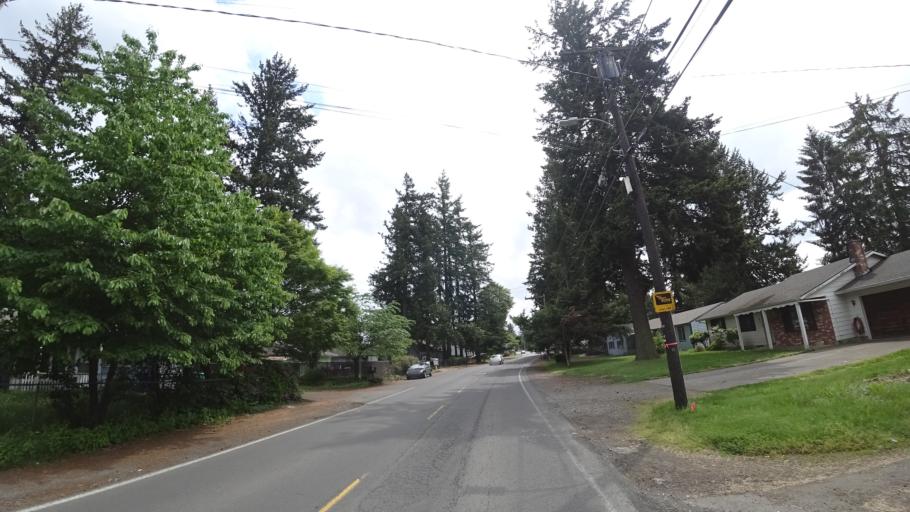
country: US
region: Oregon
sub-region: Multnomah County
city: Fairview
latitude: 45.5163
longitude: -122.4846
